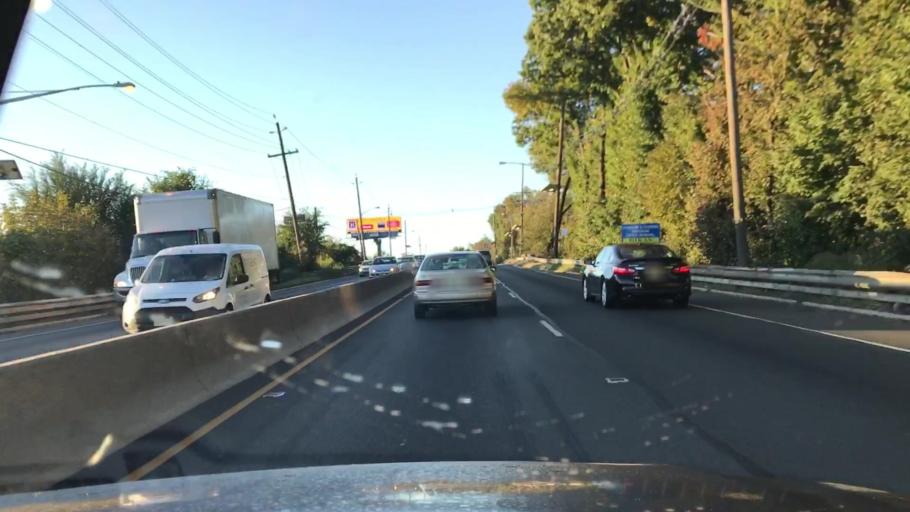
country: US
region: New Jersey
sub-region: Bergen County
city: Rochelle Park
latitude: 40.9013
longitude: -74.0727
